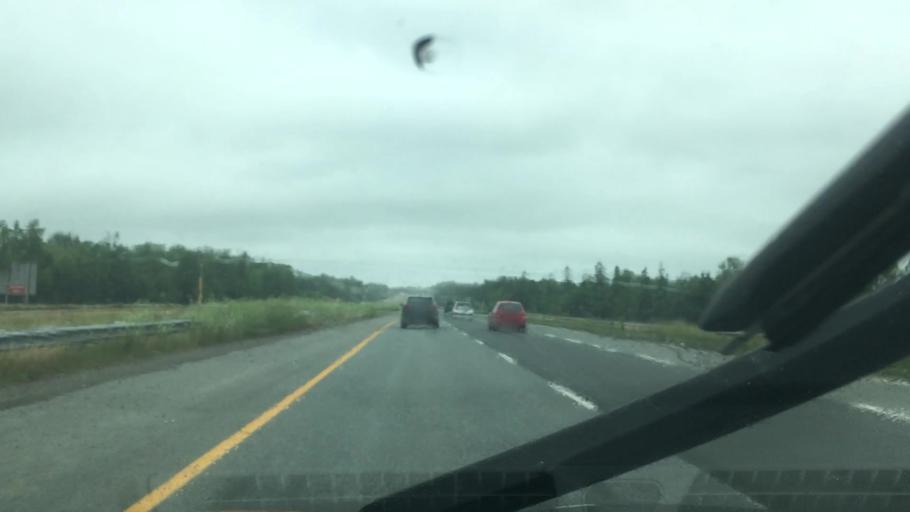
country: CA
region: Nova Scotia
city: Truro
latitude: 45.2516
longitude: -63.2921
